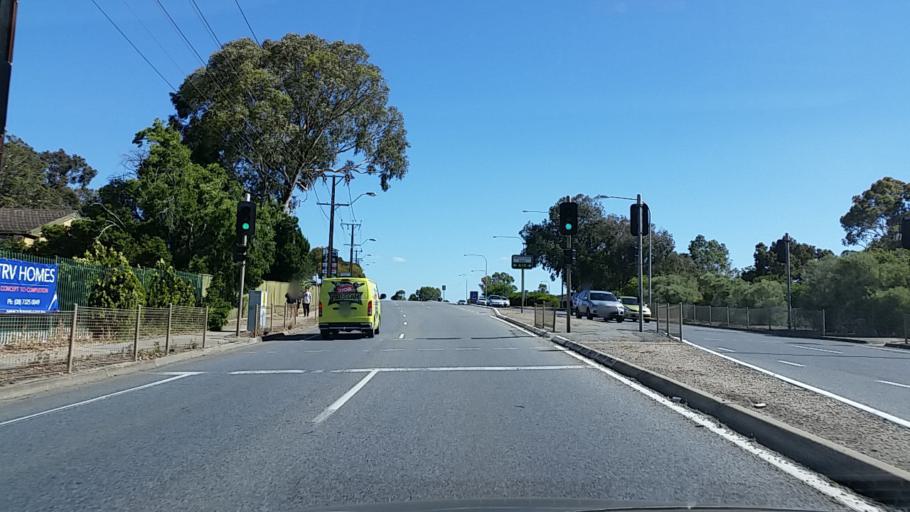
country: AU
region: South Australia
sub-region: Tea Tree Gully
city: Hope Valley
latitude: -34.8256
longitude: 138.6937
